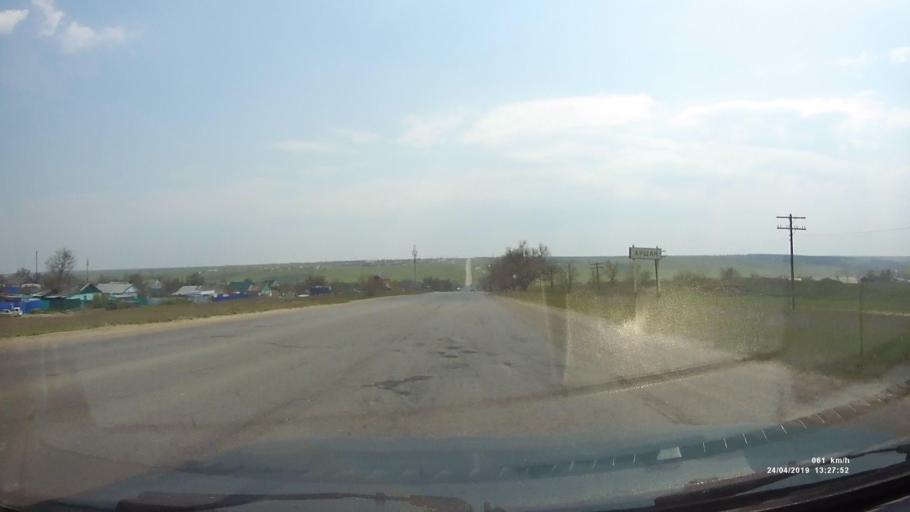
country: RU
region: Kalmykiya
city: Arshan'
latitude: 46.2772
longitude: 44.2281
